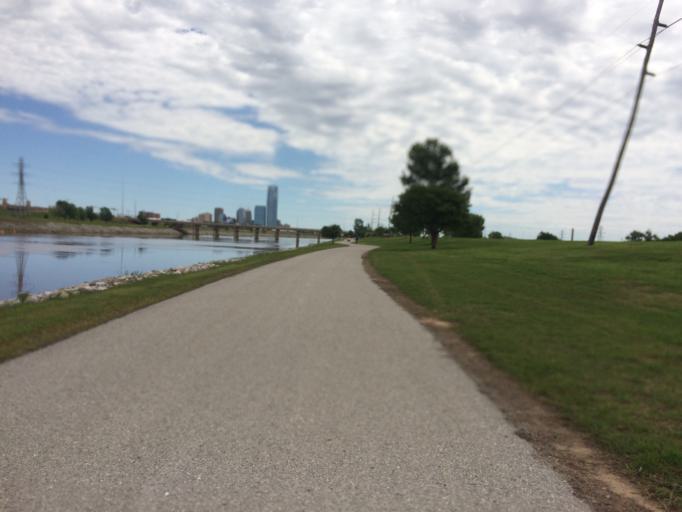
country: US
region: Oklahoma
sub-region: Oklahoma County
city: Oklahoma City
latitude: 35.4587
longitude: -97.5534
